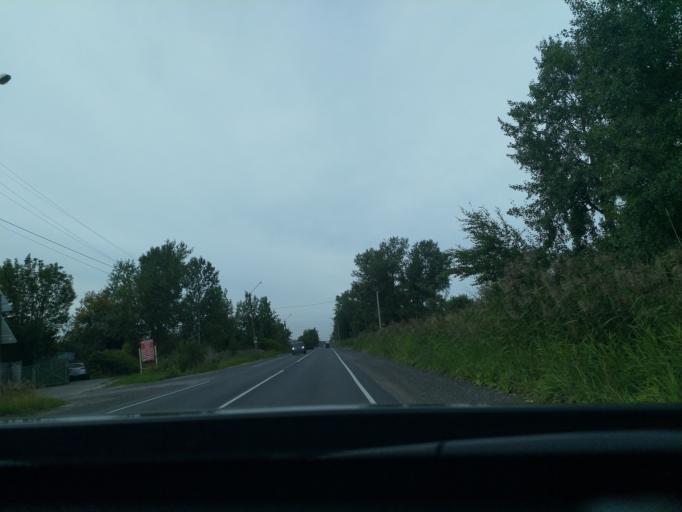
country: RU
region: Leningrad
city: Nikol'skoye
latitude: 59.7120
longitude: 30.7797
